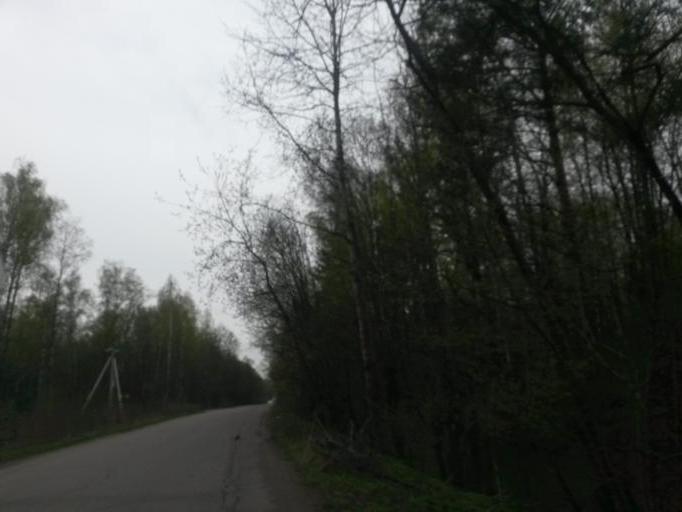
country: RU
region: Moskovskaya
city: Lyubuchany
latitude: 55.3139
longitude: 37.6160
